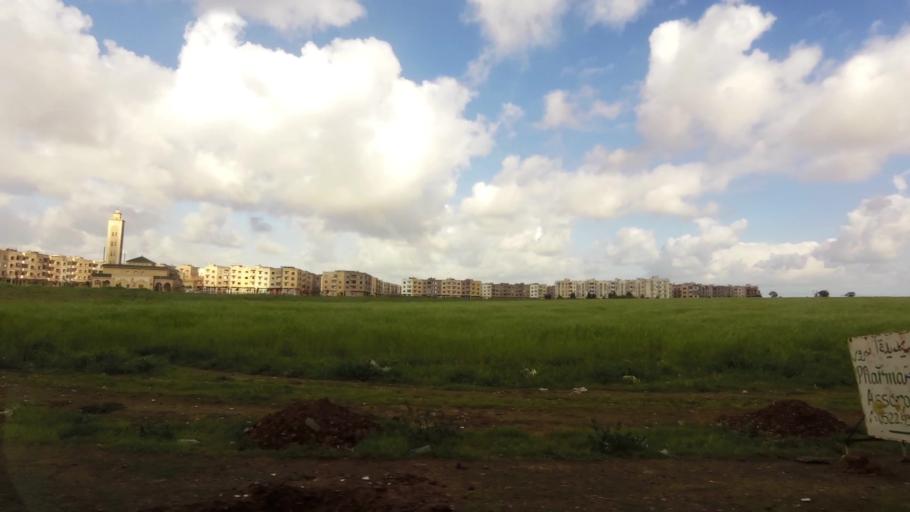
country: MA
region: Grand Casablanca
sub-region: Nouaceur
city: Bouskoura
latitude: 33.5337
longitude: -7.6993
